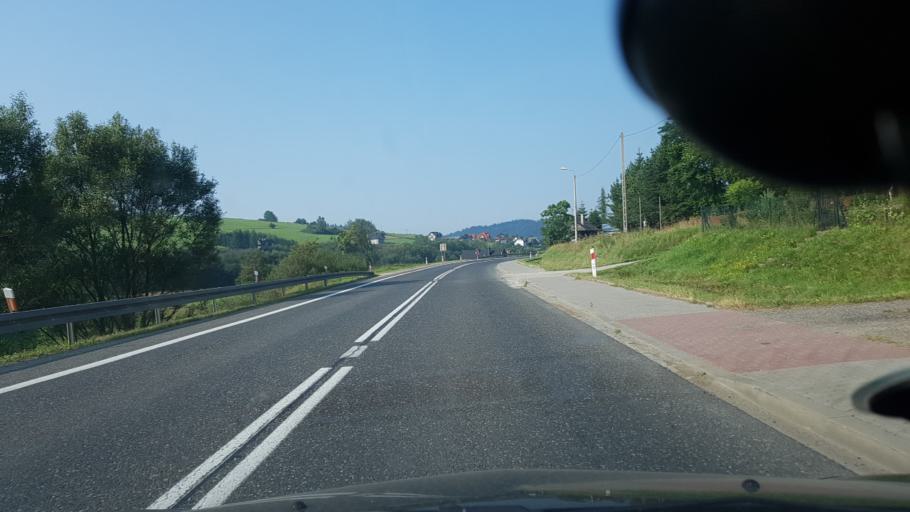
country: PL
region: Lesser Poland Voivodeship
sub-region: Powiat nowotarski
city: Podwilk
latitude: 49.5440
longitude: 19.7323
